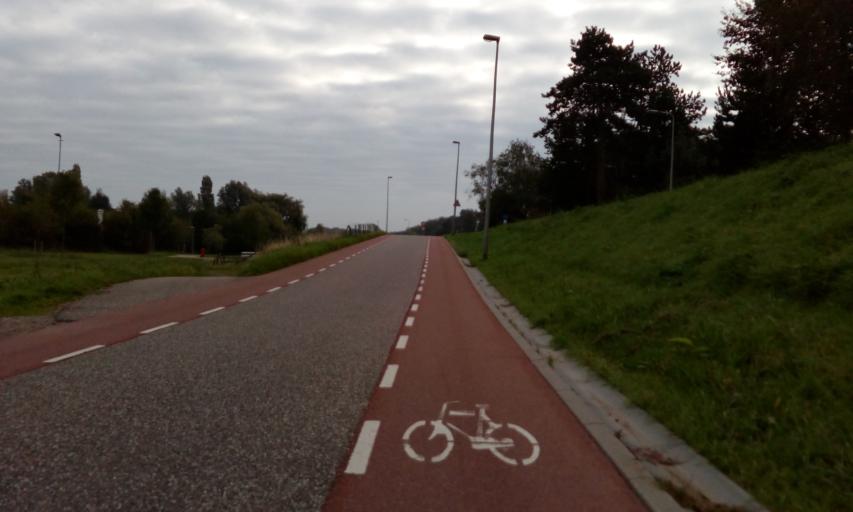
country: NL
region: South Holland
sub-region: Gemeente Albrandswaard
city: Rhoon
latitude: 51.8477
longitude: 4.4019
